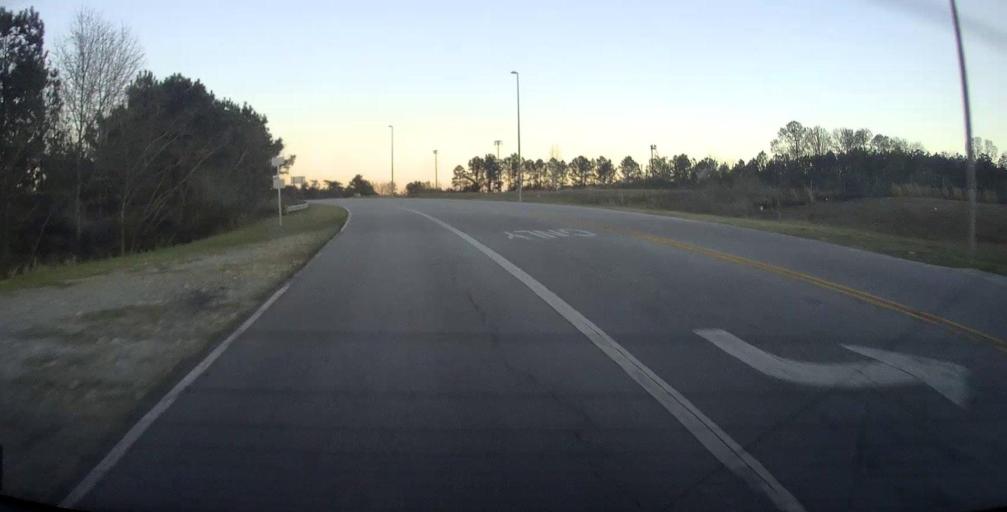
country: US
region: Alabama
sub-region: Russell County
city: Phenix City
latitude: 32.5039
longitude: -85.0033
